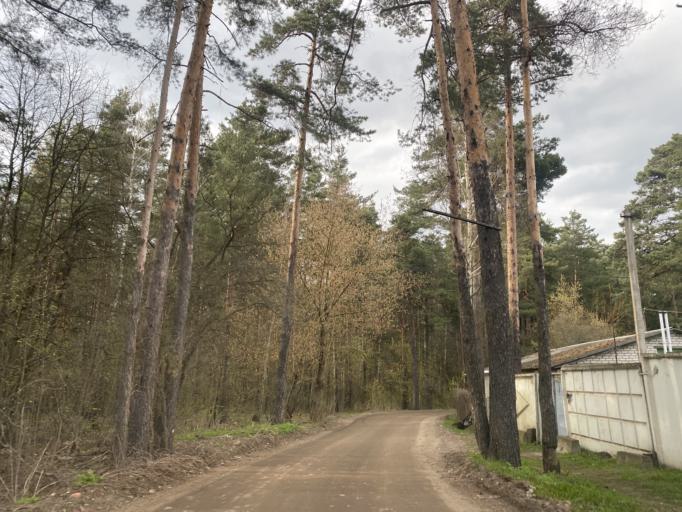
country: BY
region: Minsk
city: Vyaliki Trastsyanets
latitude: 53.9153
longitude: 27.6625
